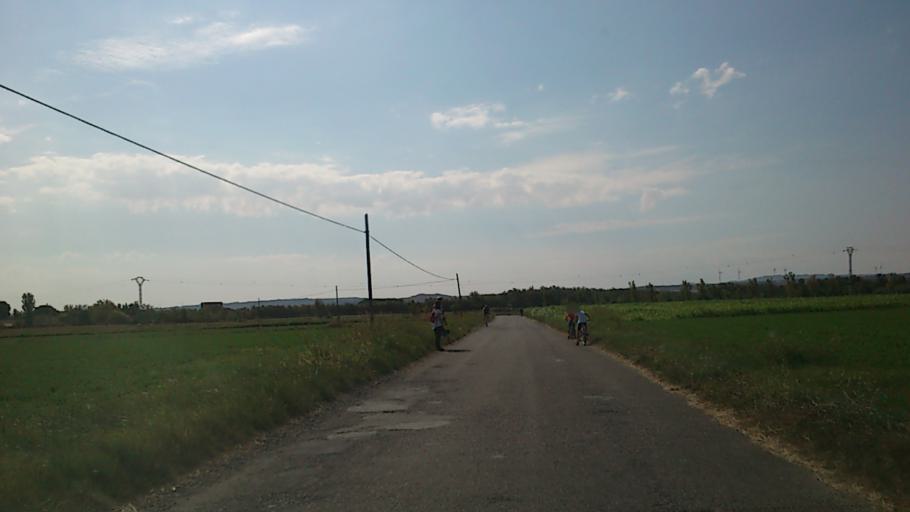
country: ES
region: Aragon
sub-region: Provincia de Zaragoza
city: Puebla de Alfinden
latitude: 41.6119
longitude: -0.7599
